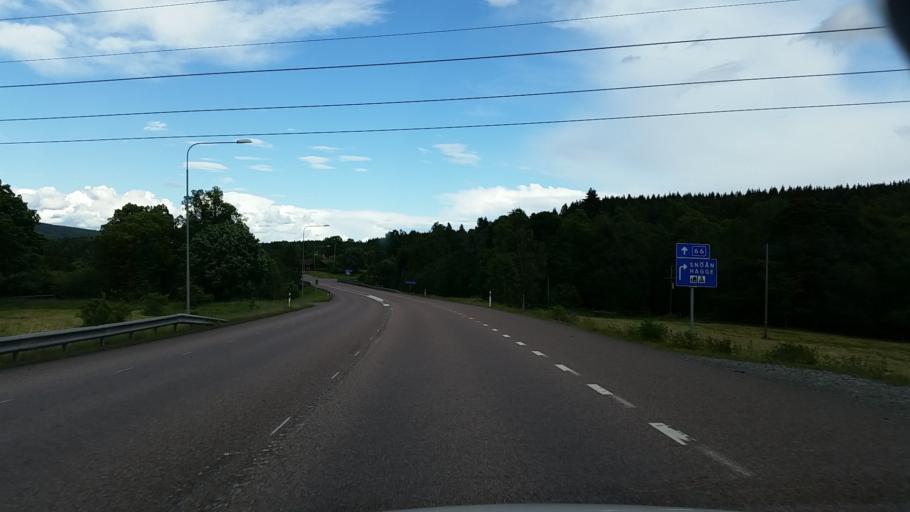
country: SE
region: Dalarna
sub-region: Smedjebackens Kommun
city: Smedjebacken
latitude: 60.1391
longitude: 15.3140
